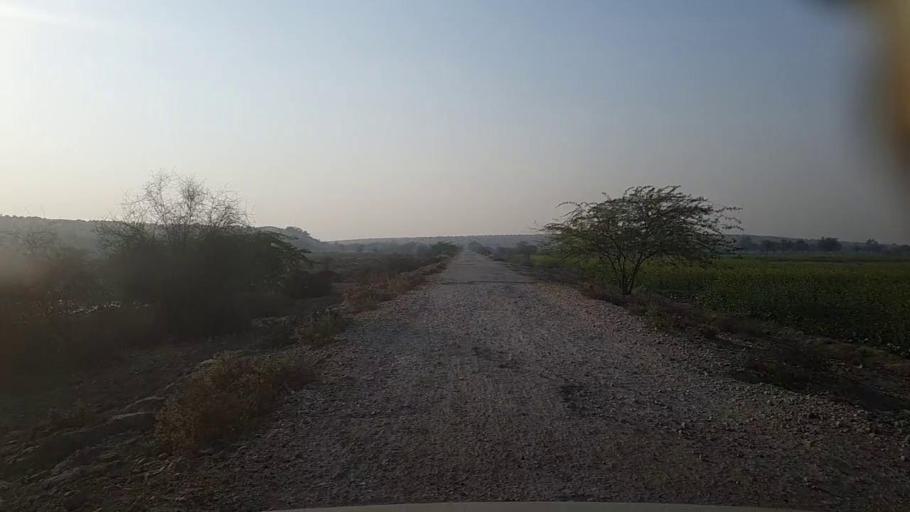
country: PK
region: Sindh
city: Pad Idan
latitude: 26.7221
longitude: 68.4456
